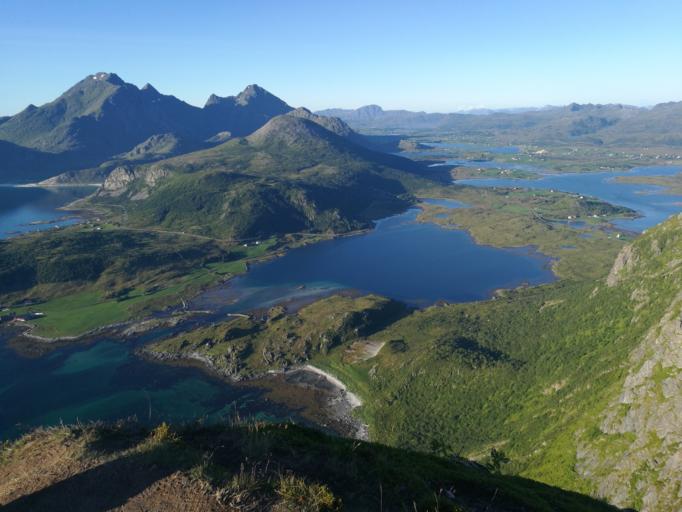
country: NO
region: Nordland
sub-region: Vestvagoy
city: Gravdal
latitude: 68.1613
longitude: 13.5019
